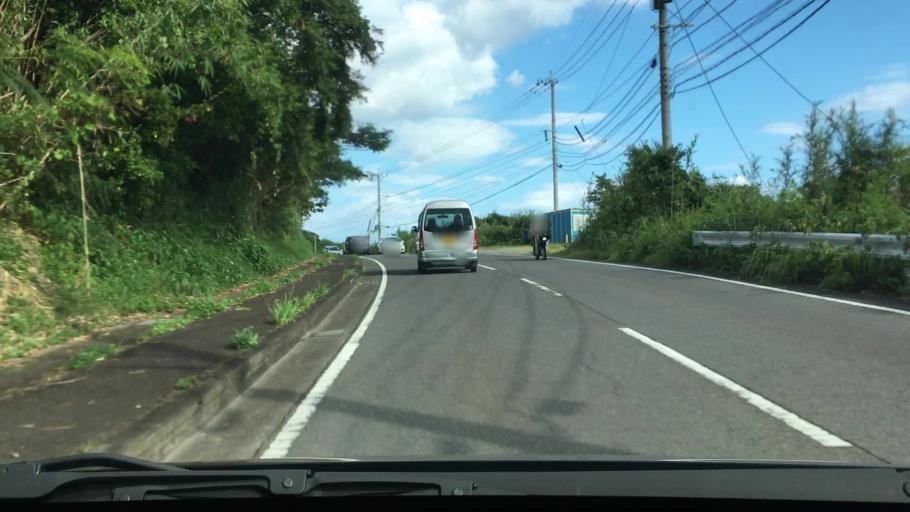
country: JP
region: Nagasaki
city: Togitsu
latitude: 32.8203
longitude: 129.7354
